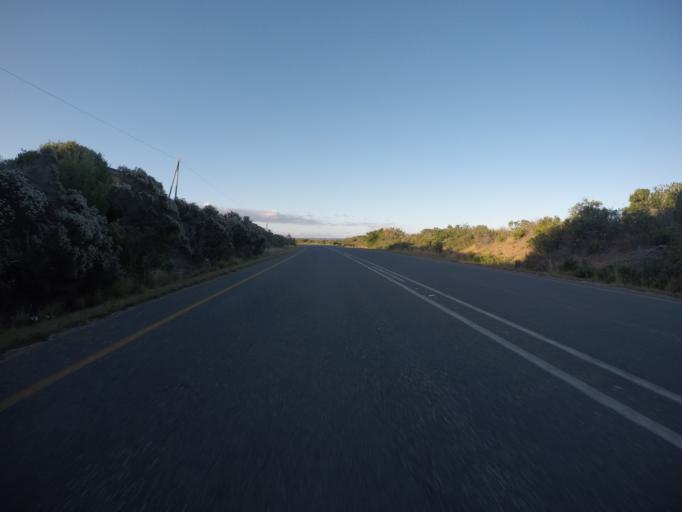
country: ZA
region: Western Cape
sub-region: Eden District Municipality
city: Riversdale
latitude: -34.3870
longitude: 21.4022
